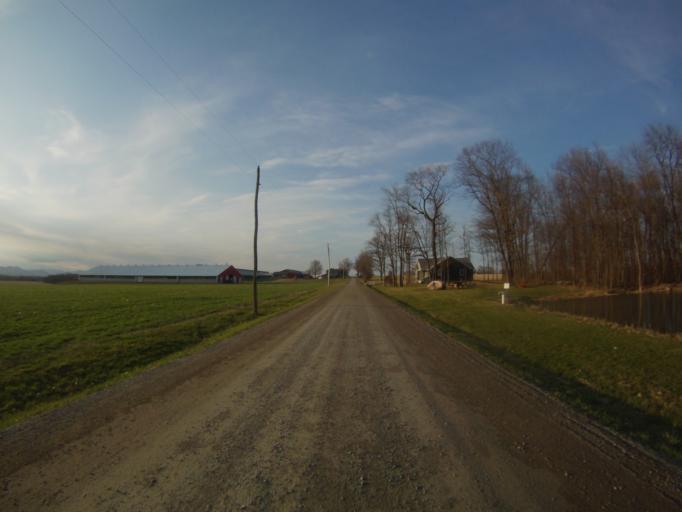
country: US
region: Vermont
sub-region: Addison County
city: Vergennes
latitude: 44.0896
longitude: -73.3110
